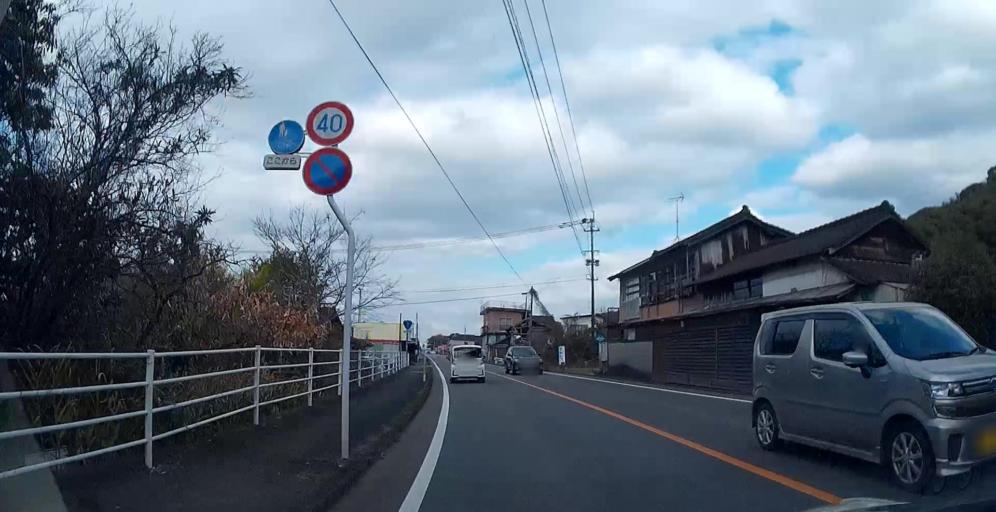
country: JP
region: Kumamoto
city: Yatsushiro
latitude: 32.4402
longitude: 130.5856
